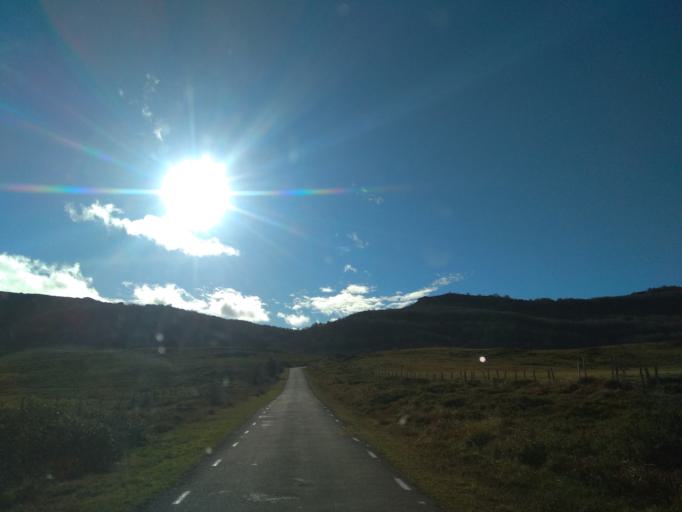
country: ES
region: Cantabria
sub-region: Provincia de Cantabria
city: San Martin de Elines
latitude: 42.9454
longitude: -3.8227
